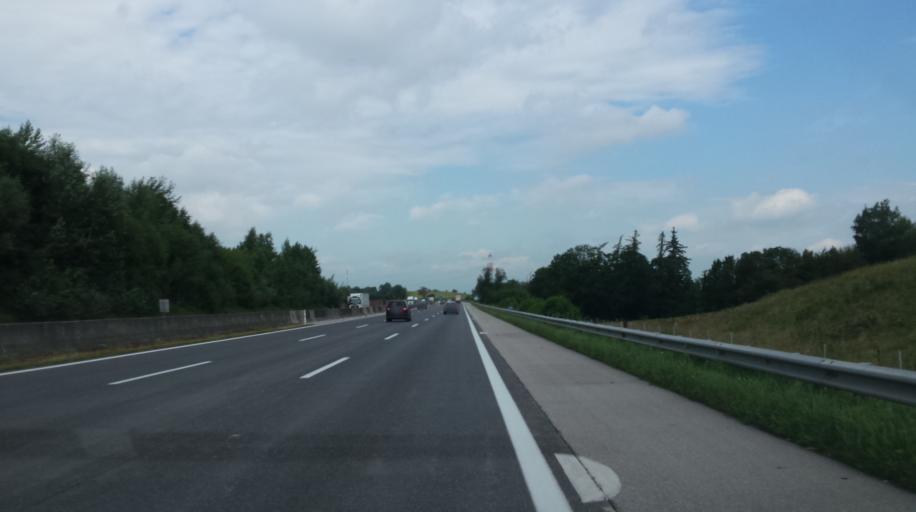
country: AT
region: Lower Austria
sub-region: Politischer Bezirk Amstetten
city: Strengberg
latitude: 48.1240
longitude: 14.6143
